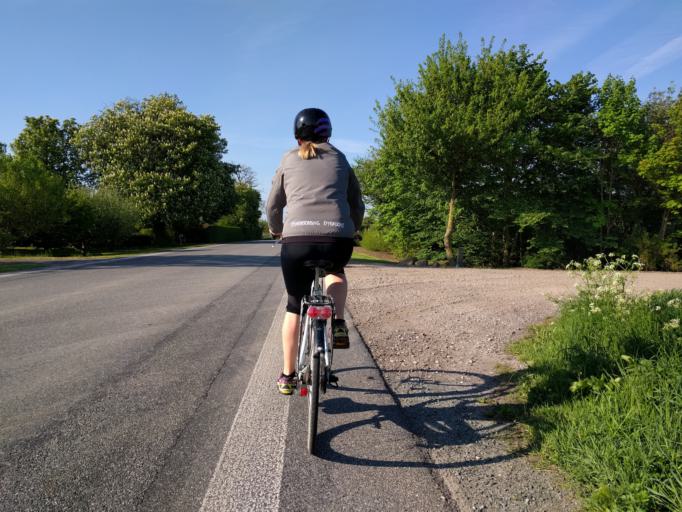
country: DK
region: Zealand
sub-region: Guldborgsund Kommune
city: Stubbekobing
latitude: 54.8709
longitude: 12.0242
